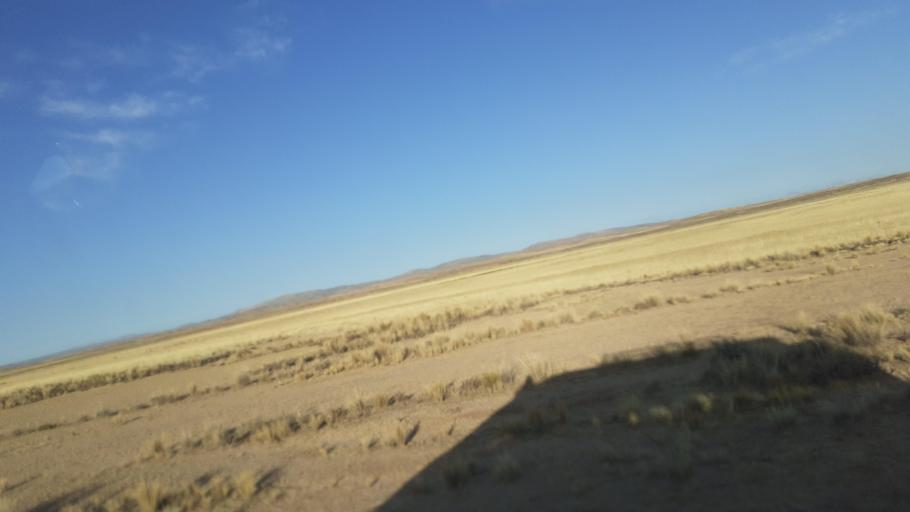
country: BO
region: La Paz
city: Tiahuanaco
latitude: -16.9471
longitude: -68.7622
